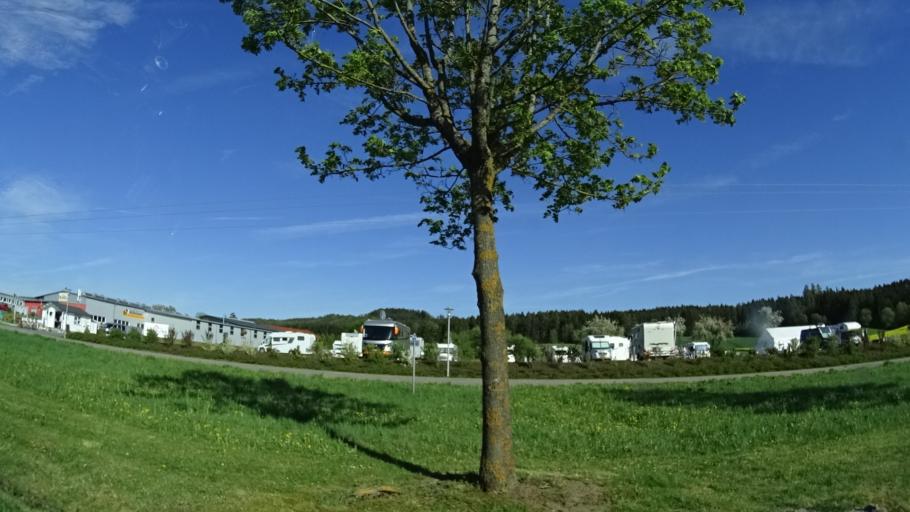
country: DE
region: Baden-Wuerttemberg
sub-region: Freiburg Region
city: Dietingen
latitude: 48.2003
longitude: 8.6455
